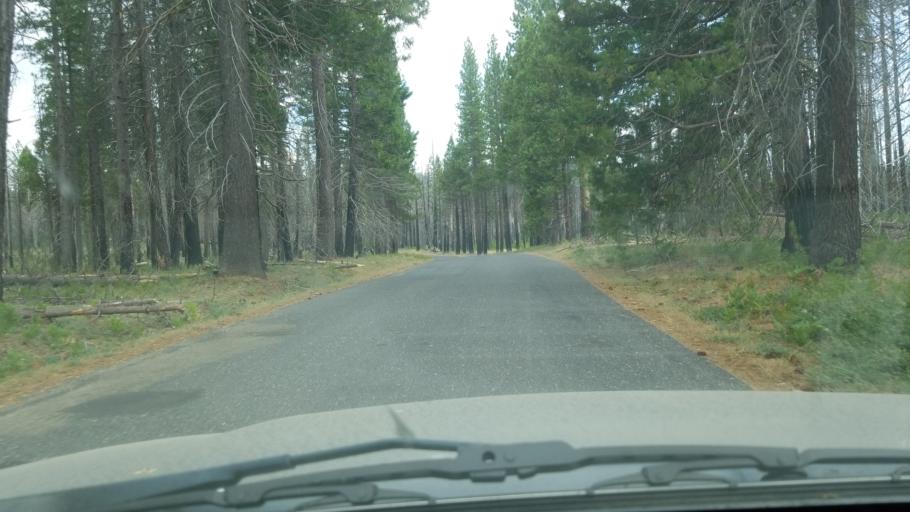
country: US
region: California
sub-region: Mariposa County
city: Yosemite Valley
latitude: 37.8402
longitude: -119.8525
